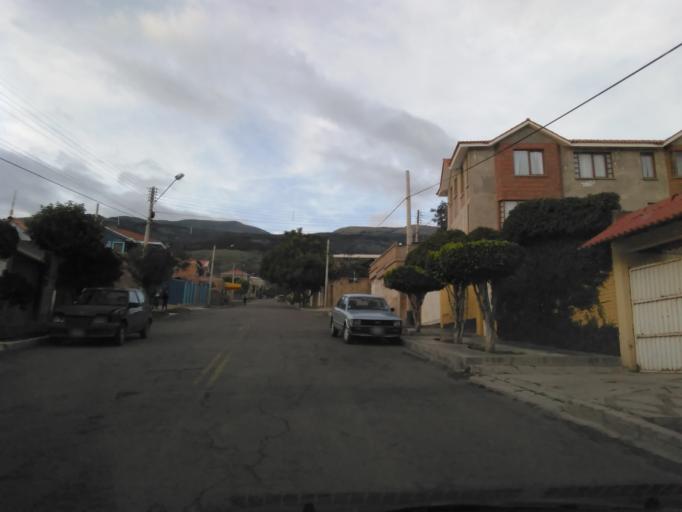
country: BO
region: Cochabamba
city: Cochabamba
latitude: -17.3579
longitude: -66.1556
